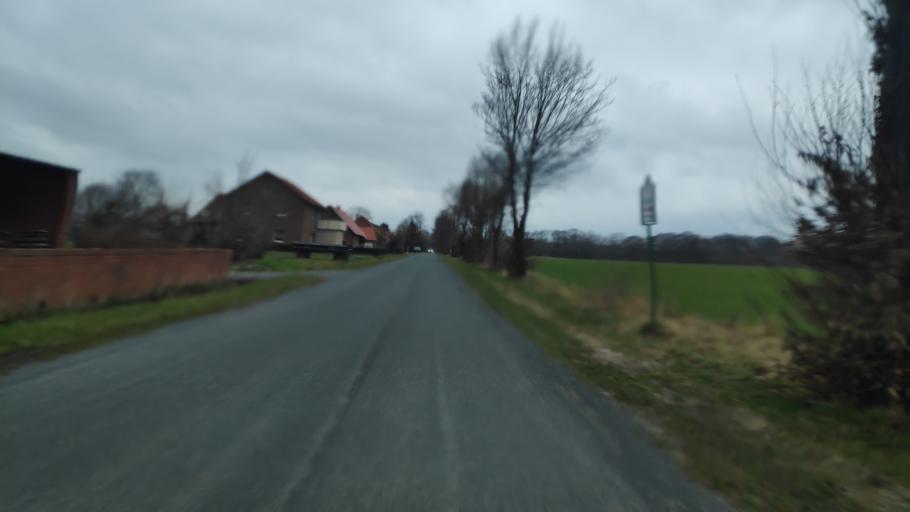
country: DE
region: North Rhine-Westphalia
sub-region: Regierungsbezirk Detmold
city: Hille
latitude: 52.3720
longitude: 8.7752
